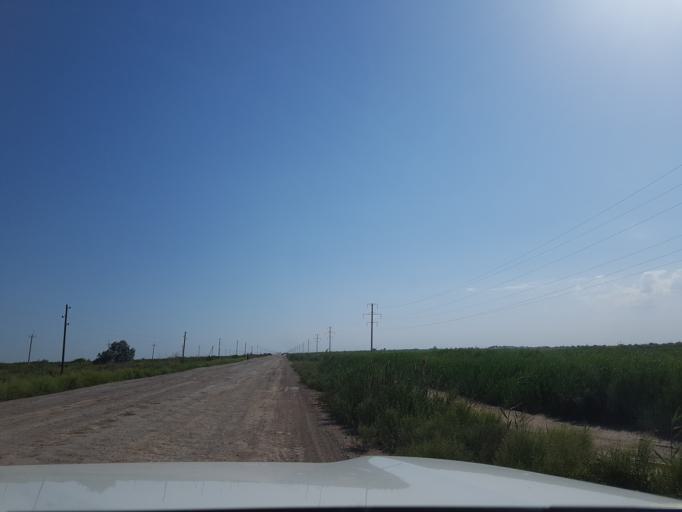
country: TM
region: Dasoguz
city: Koeneuergench
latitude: 42.1104
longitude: 58.9170
